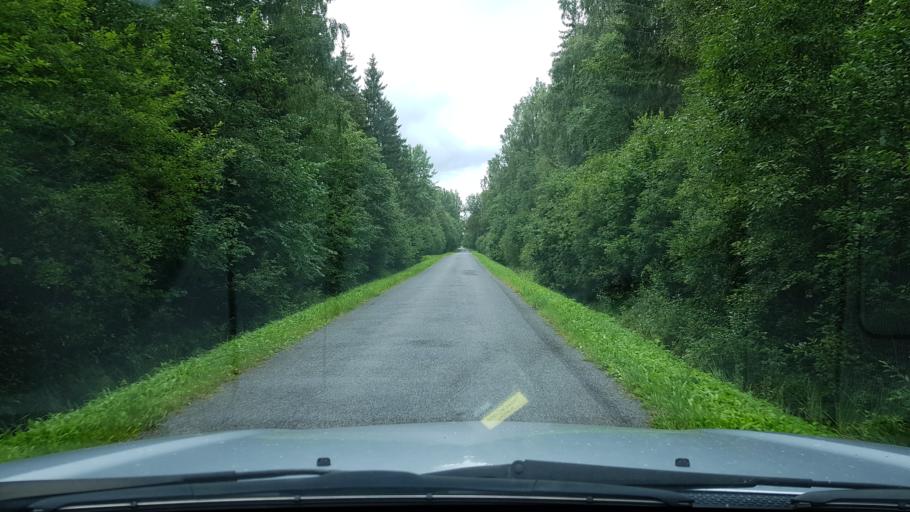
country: EE
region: Harju
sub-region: Rae vald
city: Vaida
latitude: 59.2989
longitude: 24.9979
